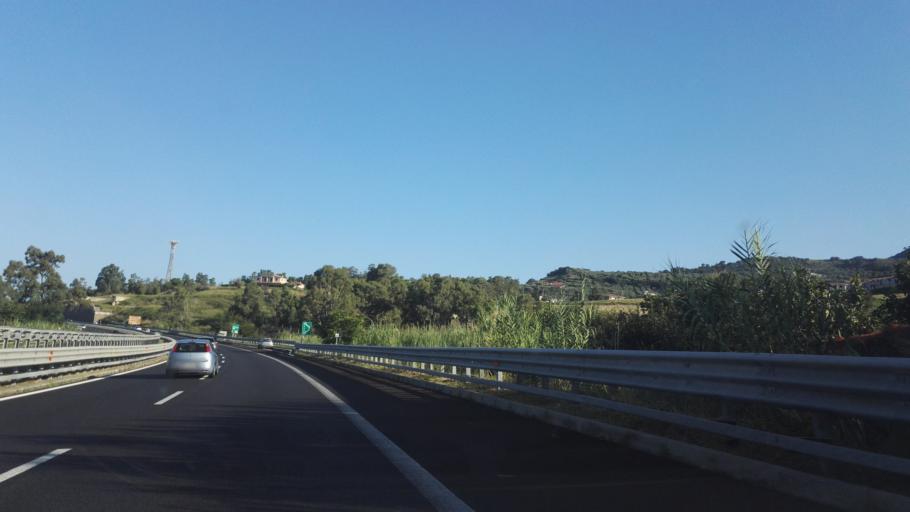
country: IT
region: Calabria
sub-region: Provincia di Catanzaro
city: Falerna Scalo
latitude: 38.9732
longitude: 16.1521
